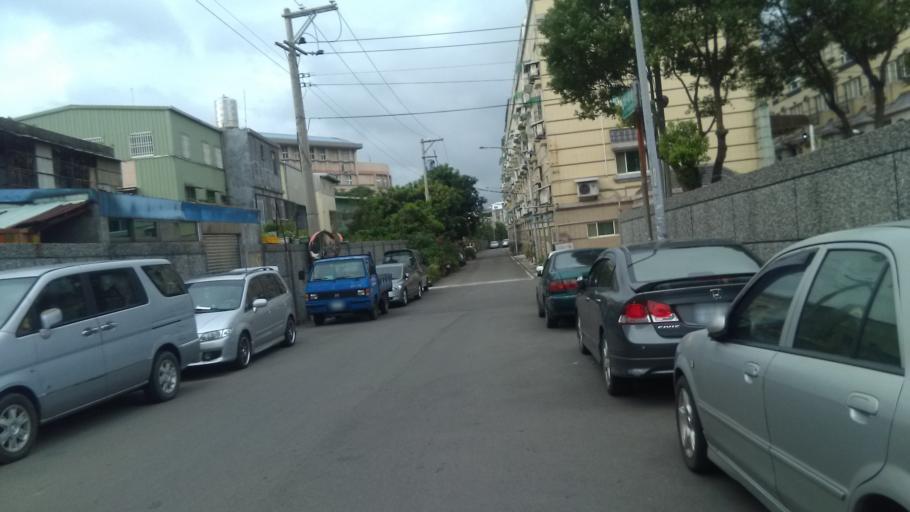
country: TW
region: Taiwan
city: Taoyuan City
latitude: 24.9525
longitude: 121.2590
